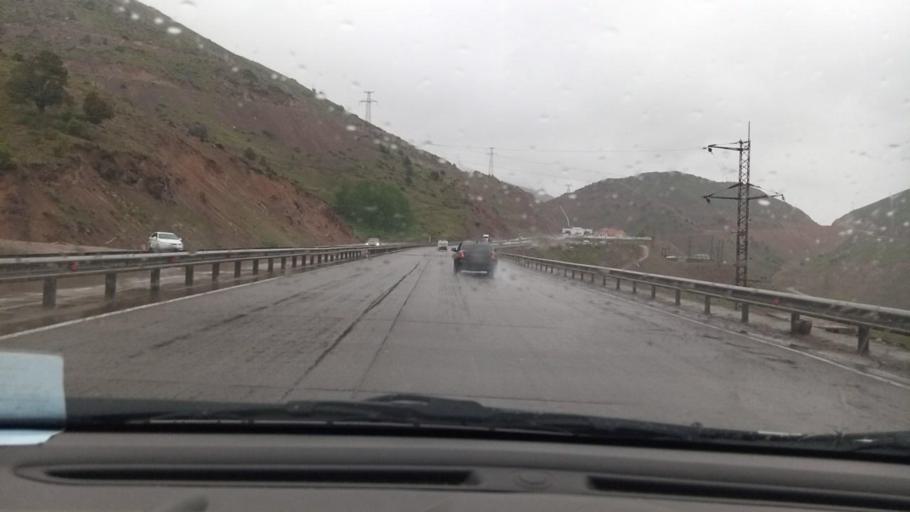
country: UZ
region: Toshkent
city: Angren
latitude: 41.0859
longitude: 70.5363
